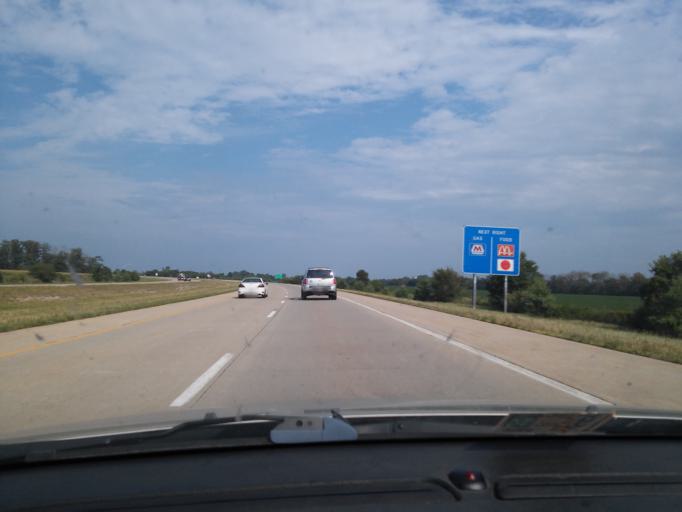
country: US
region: Ohio
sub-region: Greene County
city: Shawnee Hills
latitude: 39.6668
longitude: -83.7854
